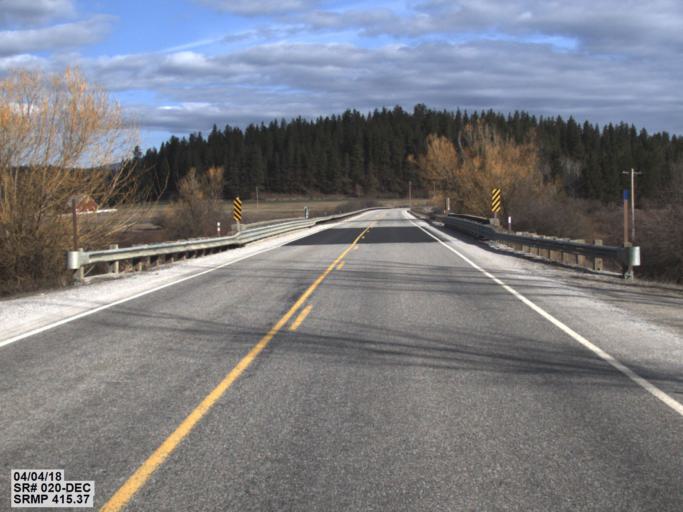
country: US
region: Washington
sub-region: Pend Oreille County
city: Newport
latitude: 48.3893
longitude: -117.3132
